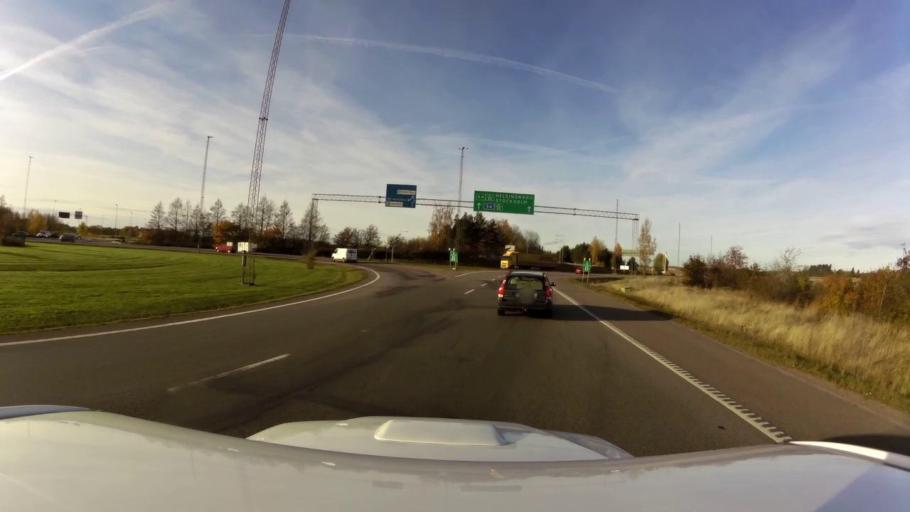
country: SE
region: OEstergoetland
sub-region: Linkopings Kommun
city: Linkoping
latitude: 58.4243
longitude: 15.6690
